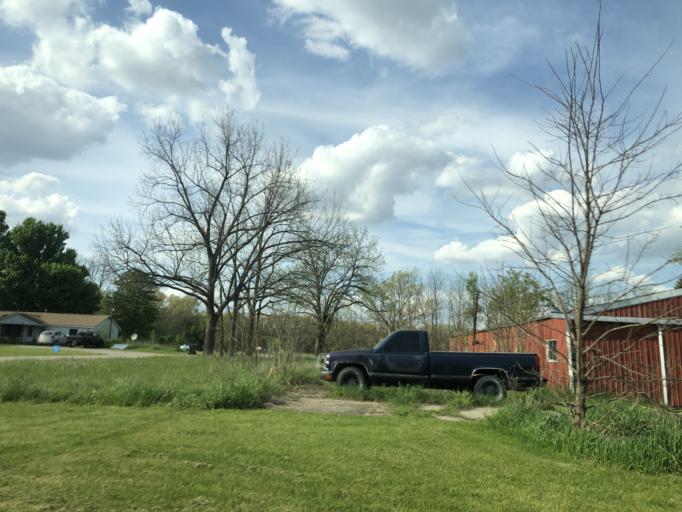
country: US
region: Michigan
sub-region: Hillsdale County
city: Reading
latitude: 41.7525
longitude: -84.8138
